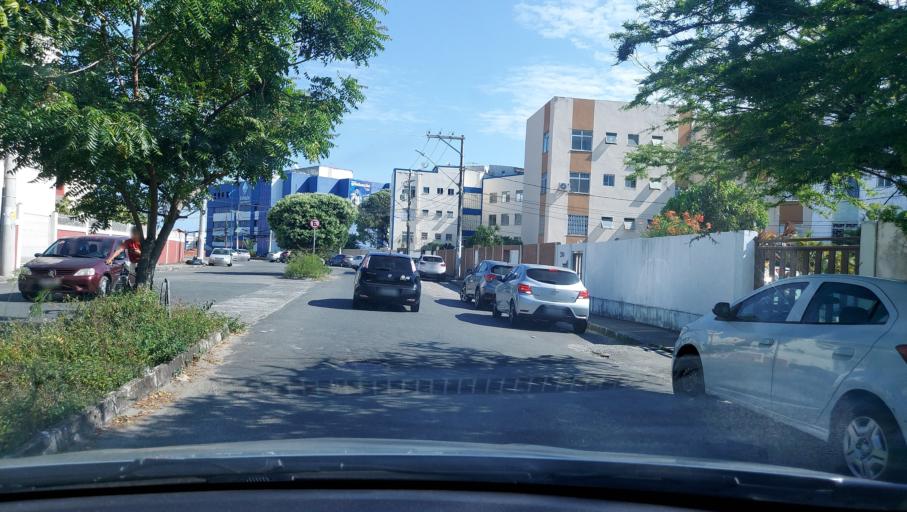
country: BR
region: Bahia
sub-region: Salvador
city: Salvador
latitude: -12.9798
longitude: -38.4465
